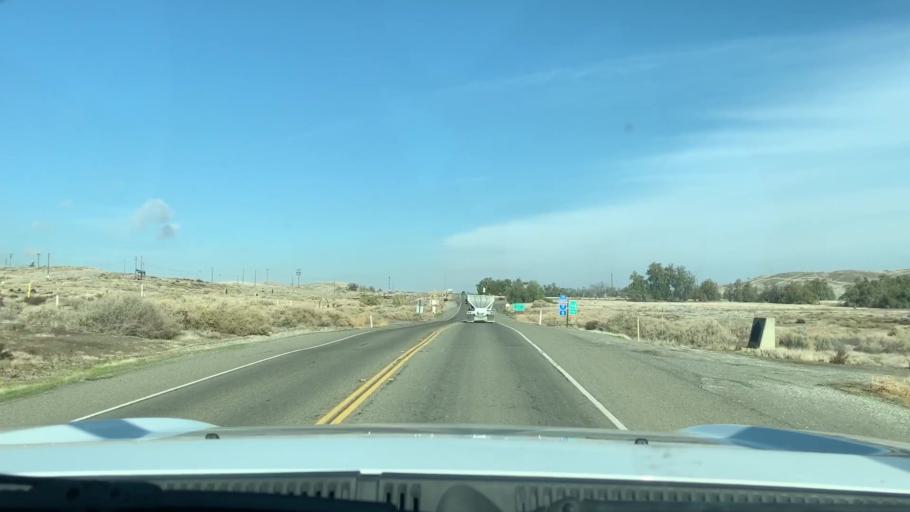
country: US
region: California
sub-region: Fresno County
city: Coalinga
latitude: 36.2440
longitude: -120.3151
